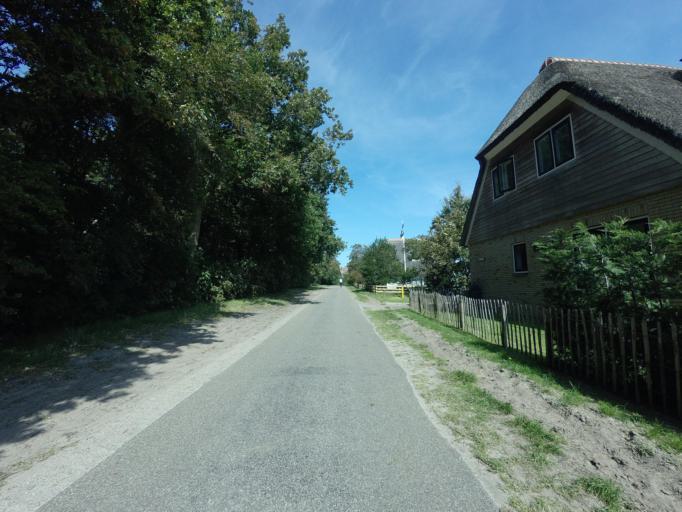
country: NL
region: Friesland
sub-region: Gemeente Ameland
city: Hollum
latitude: 53.4429
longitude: 5.6234
